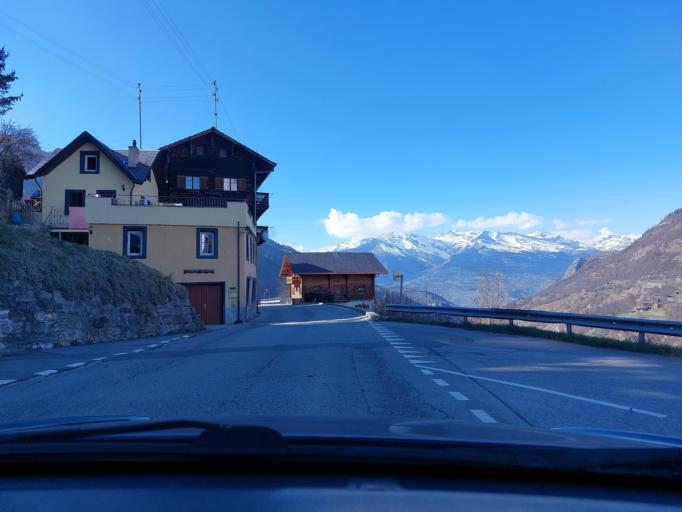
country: CH
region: Valais
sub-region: Herens District
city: Heremence
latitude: 46.1723
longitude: 7.4215
